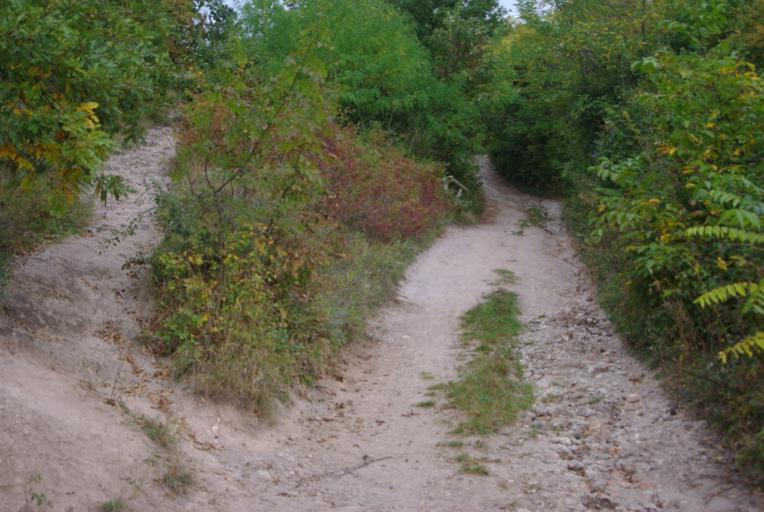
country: HU
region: Pest
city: Nagymaros
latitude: 47.7952
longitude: 18.9466
